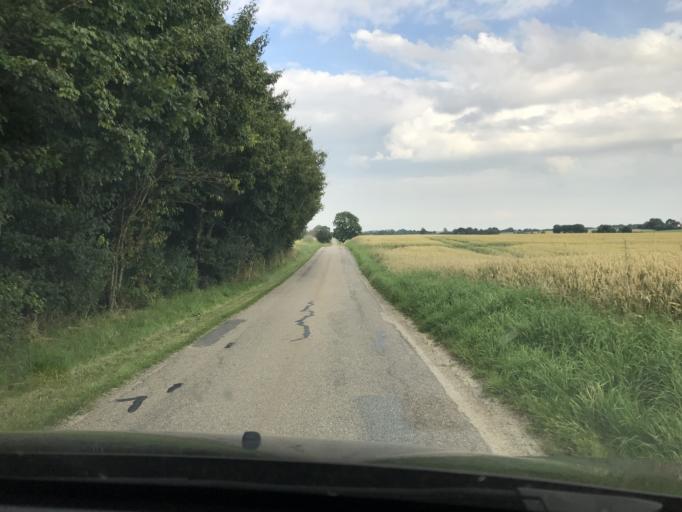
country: DK
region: South Denmark
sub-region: Vejle Kommune
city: Jelling
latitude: 55.8048
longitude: 9.4038
